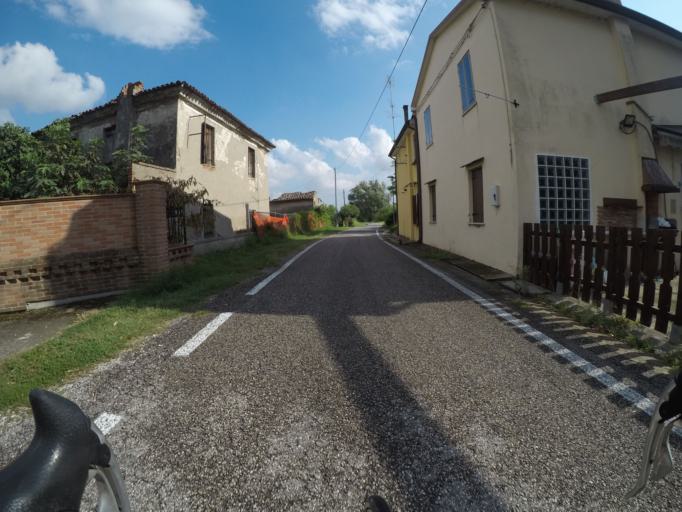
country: IT
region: Veneto
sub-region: Provincia di Rovigo
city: Villamarzana
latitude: 45.0029
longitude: 11.6828
